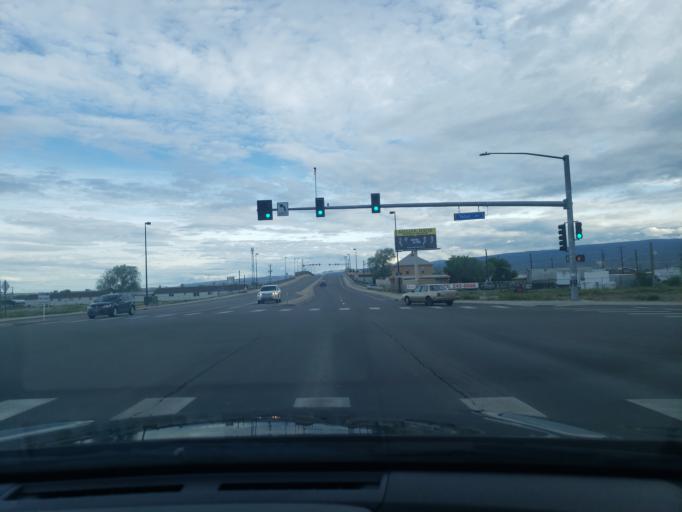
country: US
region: Colorado
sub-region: Mesa County
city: Fruitvale
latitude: 39.0755
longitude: -108.5153
